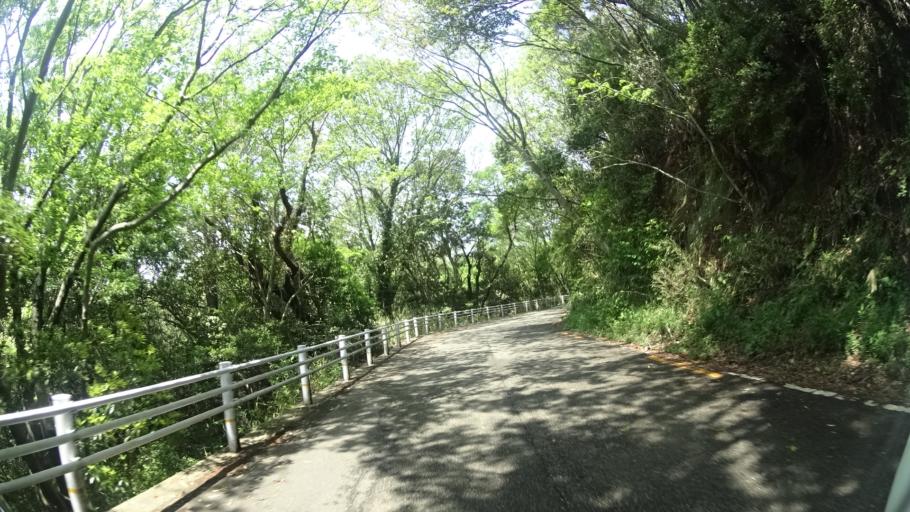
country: JP
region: Tokushima
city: Tokushima-shi
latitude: 34.0655
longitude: 134.5281
